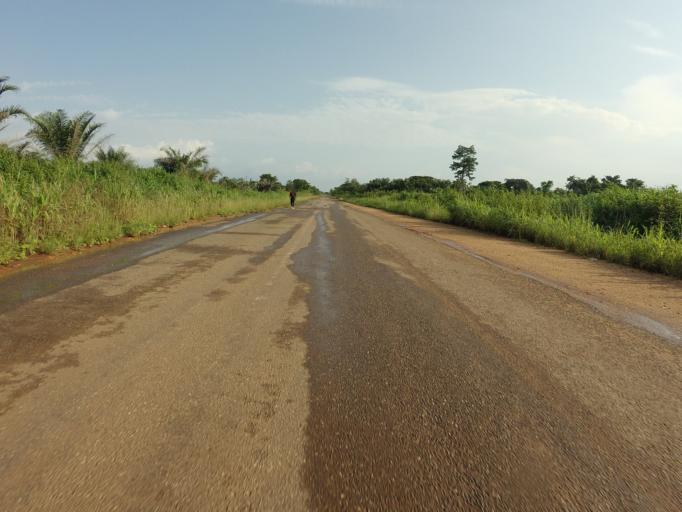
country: GH
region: Volta
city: Hohoe
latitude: 7.0708
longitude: 0.4354
